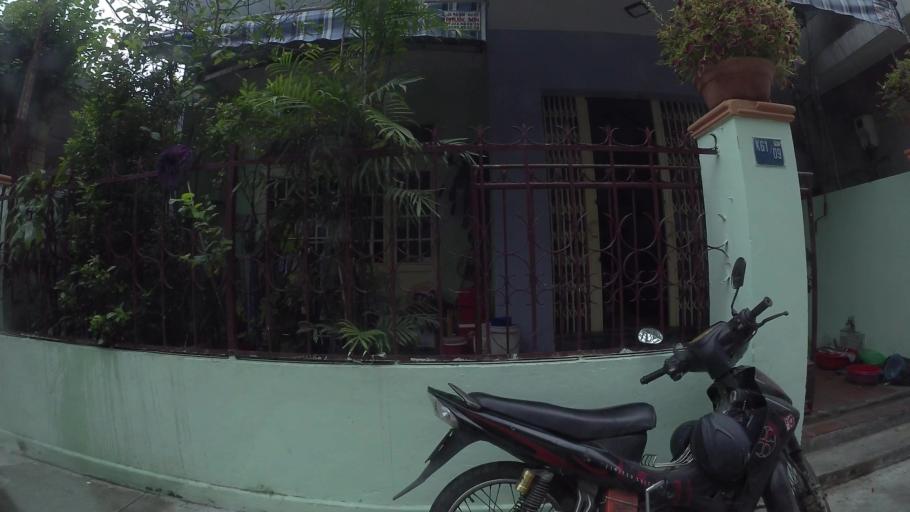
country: VN
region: Da Nang
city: Da Nang
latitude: 16.0847
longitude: 108.2200
